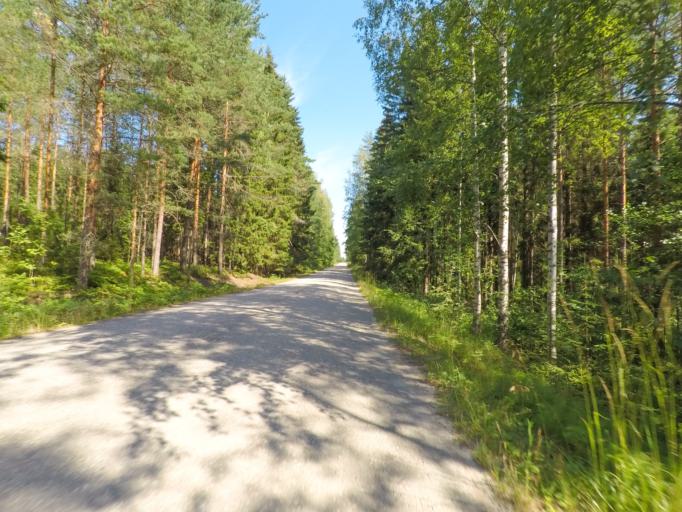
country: FI
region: Southern Savonia
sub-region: Mikkeli
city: Puumala
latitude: 61.4055
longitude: 28.0512
